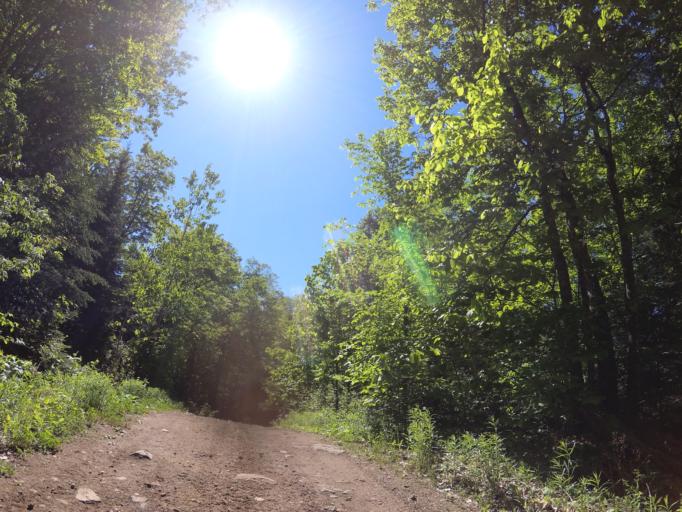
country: CA
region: Ontario
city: Renfrew
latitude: 45.0853
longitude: -77.0945
